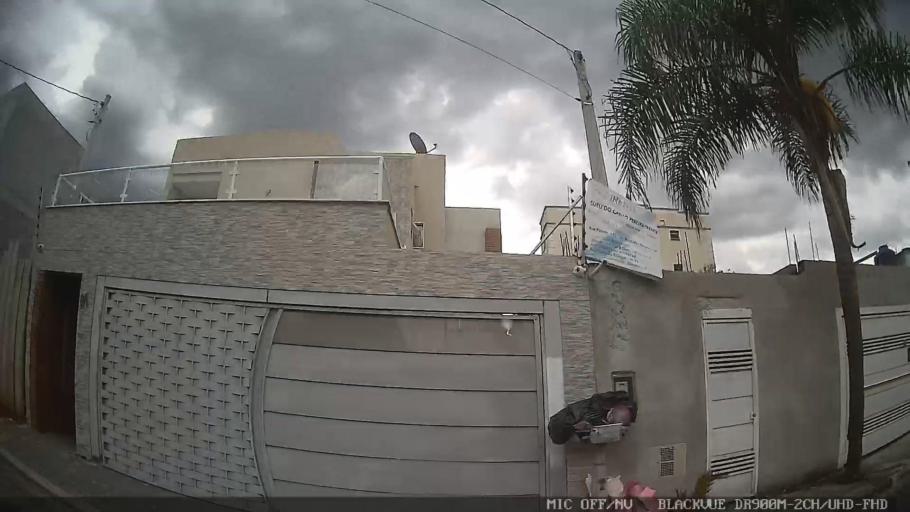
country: BR
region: Sao Paulo
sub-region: Suzano
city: Suzano
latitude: -23.5504
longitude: -46.3295
